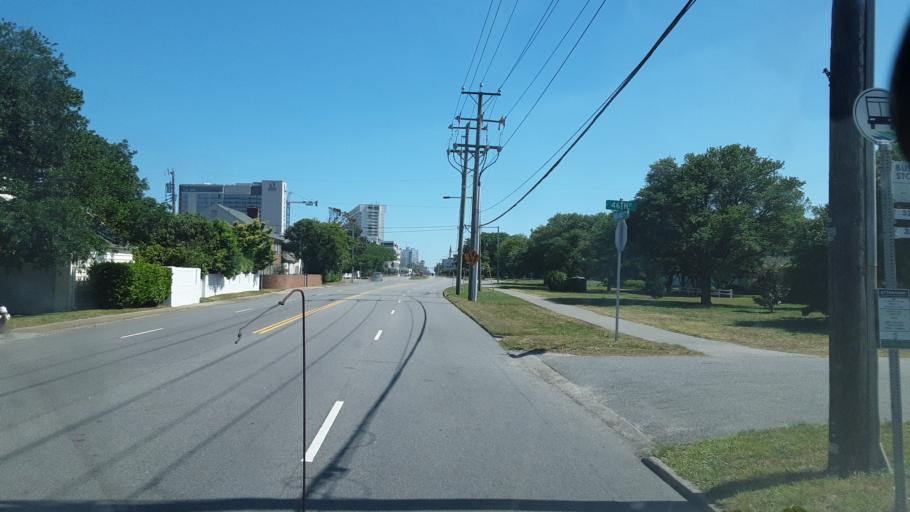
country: US
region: Virginia
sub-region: City of Virginia Beach
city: Virginia Beach
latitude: 36.8741
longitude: -75.9835
